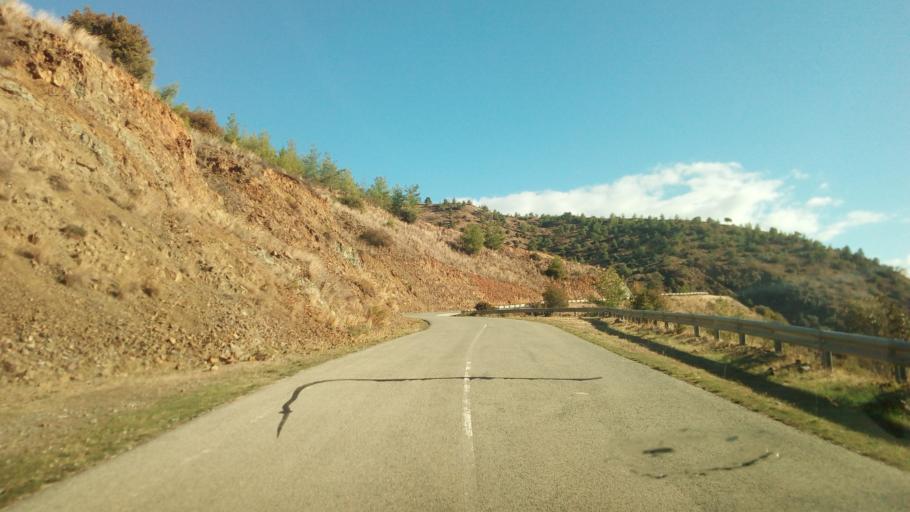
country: CY
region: Lefkosia
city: Lefka
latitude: 35.0753
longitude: 32.8040
